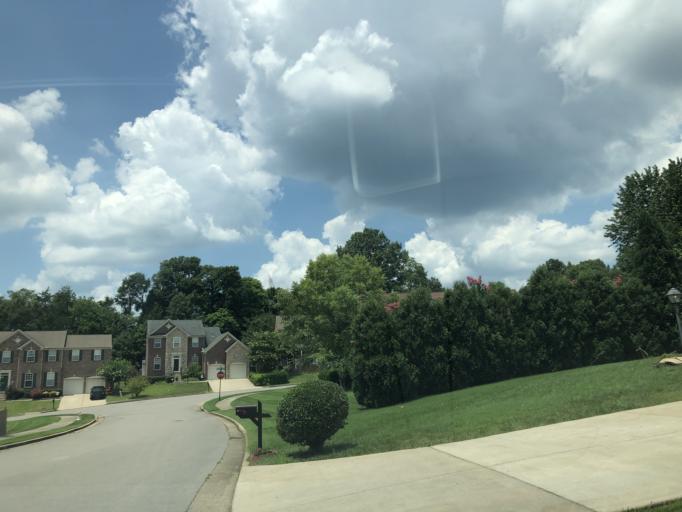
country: US
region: Tennessee
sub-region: Williamson County
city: Brentwood Estates
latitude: 36.0173
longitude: -86.7115
